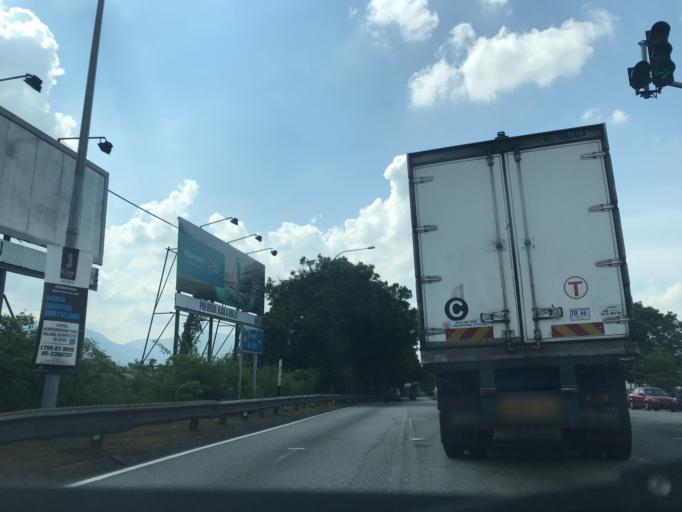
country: MY
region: Perak
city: Ipoh
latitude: 4.6255
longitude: 101.1154
